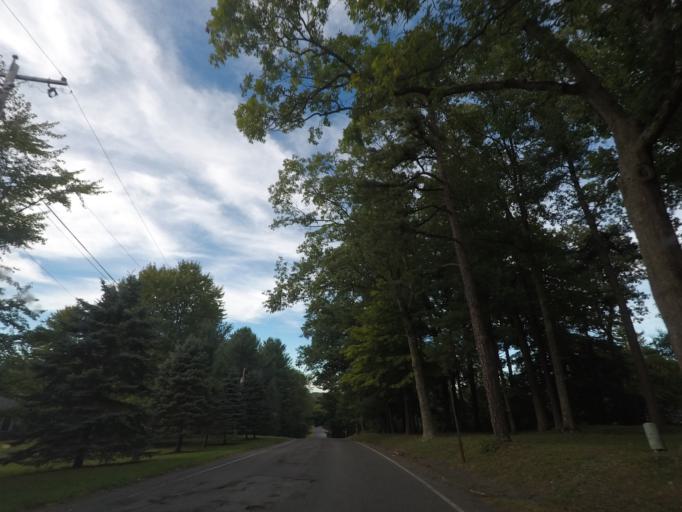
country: US
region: New York
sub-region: Rensselaer County
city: East Greenbush
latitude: 42.6105
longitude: -73.6759
